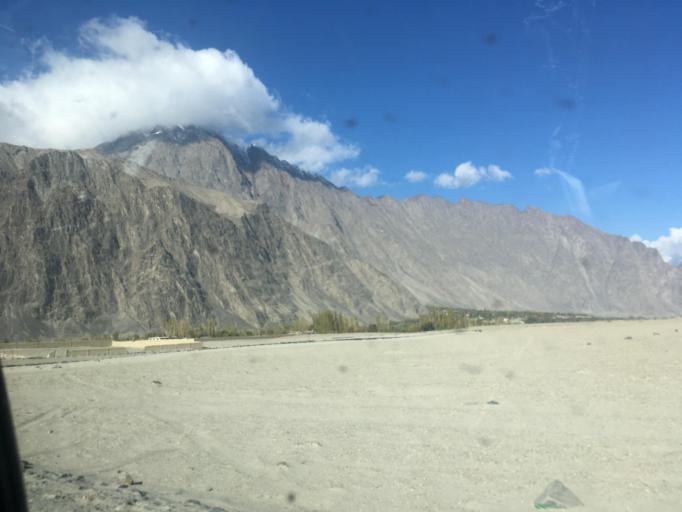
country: PK
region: Gilgit-Baltistan
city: Skardu
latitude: 35.3558
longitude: 75.5239
